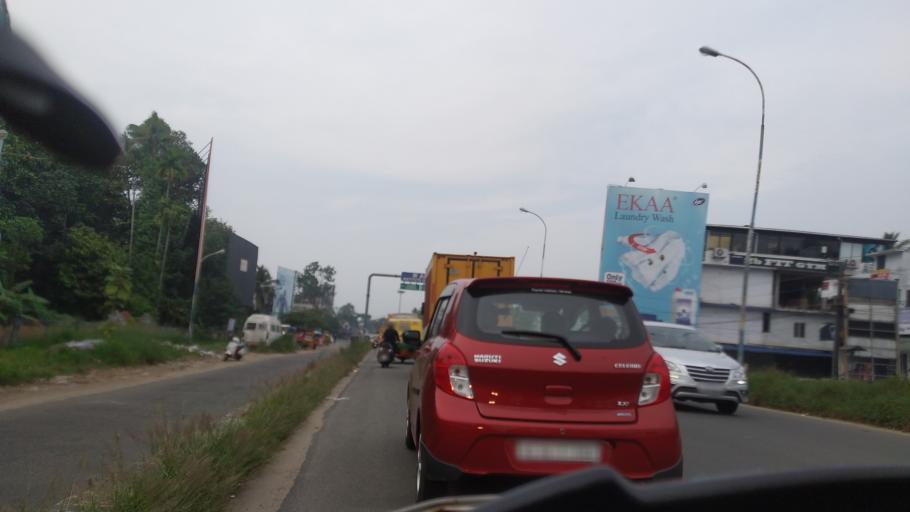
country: IN
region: Kerala
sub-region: Ernakulam
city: Elur
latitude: 10.0420
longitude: 76.2996
